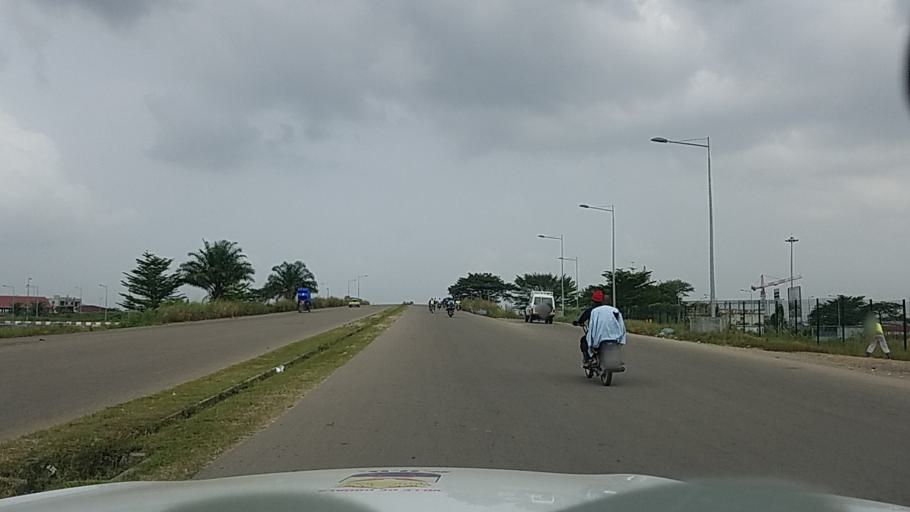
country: CM
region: Littoral
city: Douala
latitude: 4.0184
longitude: 9.7187
